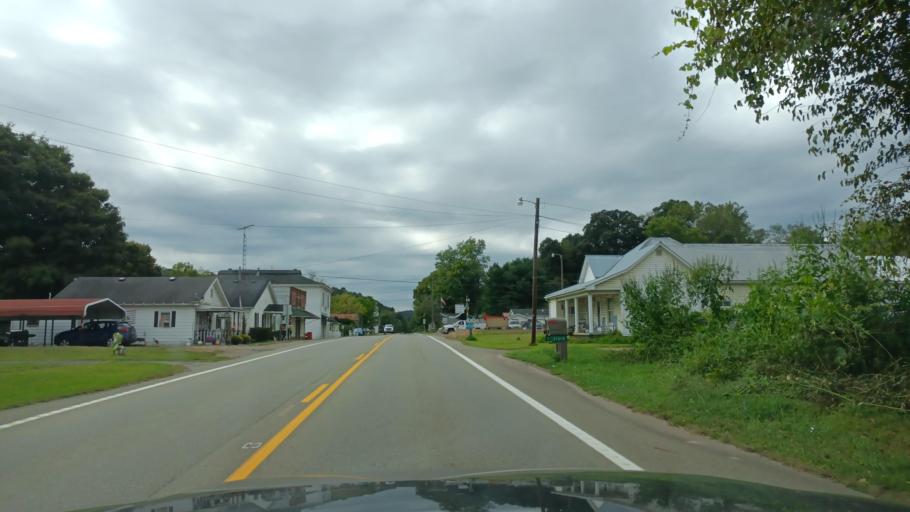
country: US
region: Ohio
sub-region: Vinton County
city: McArthur
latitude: 39.2726
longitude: -82.6056
